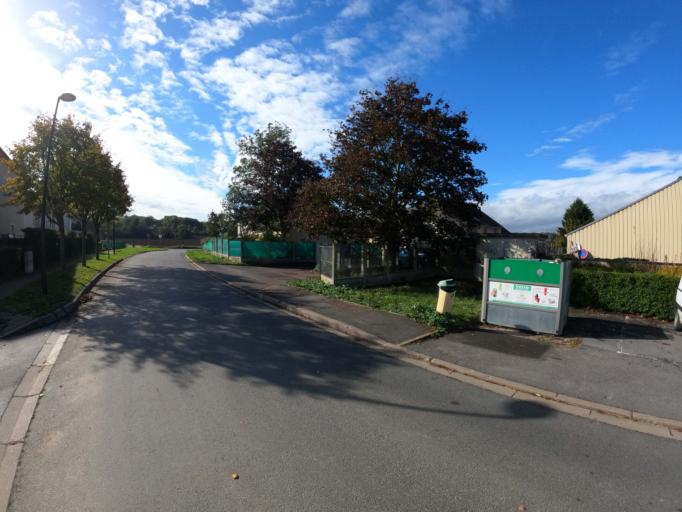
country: FR
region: Ile-de-France
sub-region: Departement de Seine-et-Marne
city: Saint-Germain-sur-Morin
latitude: 48.8789
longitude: 2.8456
